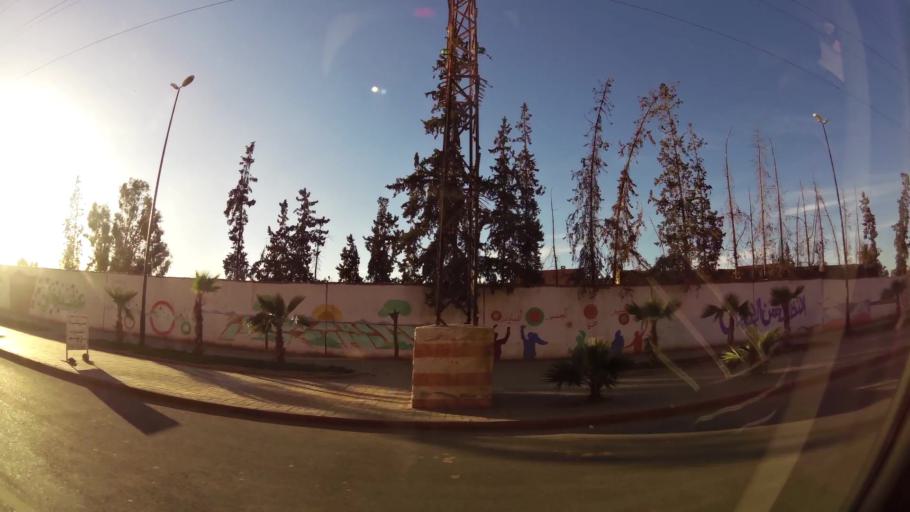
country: MA
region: Marrakech-Tensift-Al Haouz
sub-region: Marrakech
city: Marrakesh
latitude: 31.6194
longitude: -8.0527
